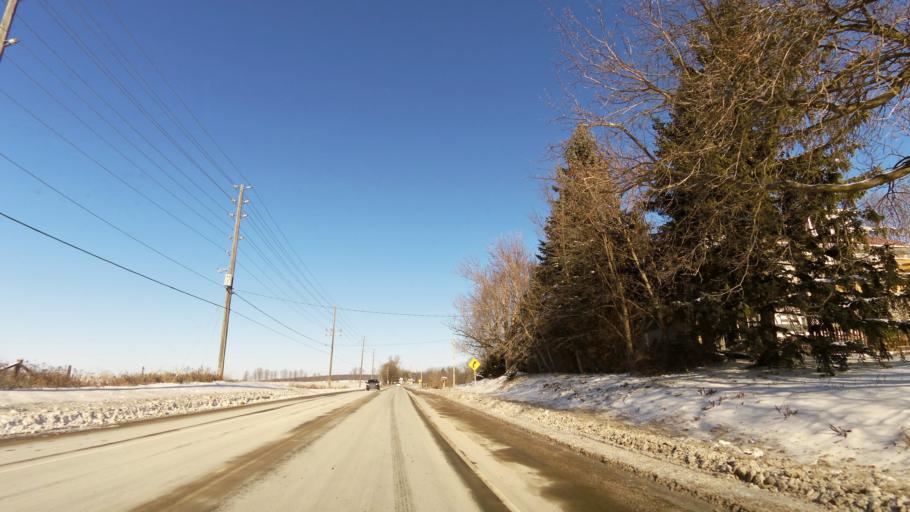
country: CA
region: Ontario
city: Quinte West
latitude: 44.2136
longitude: -77.8264
